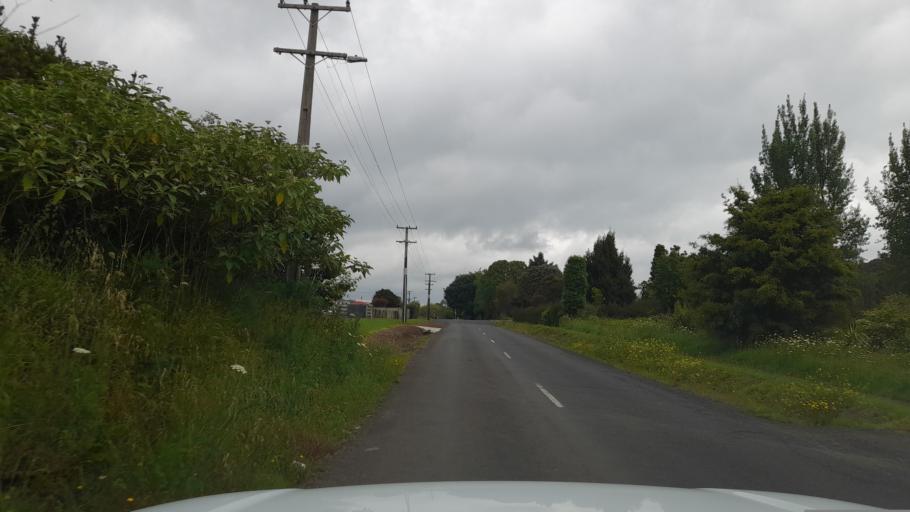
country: NZ
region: Northland
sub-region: Far North District
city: Waimate North
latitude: -35.4029
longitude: 173.7871
